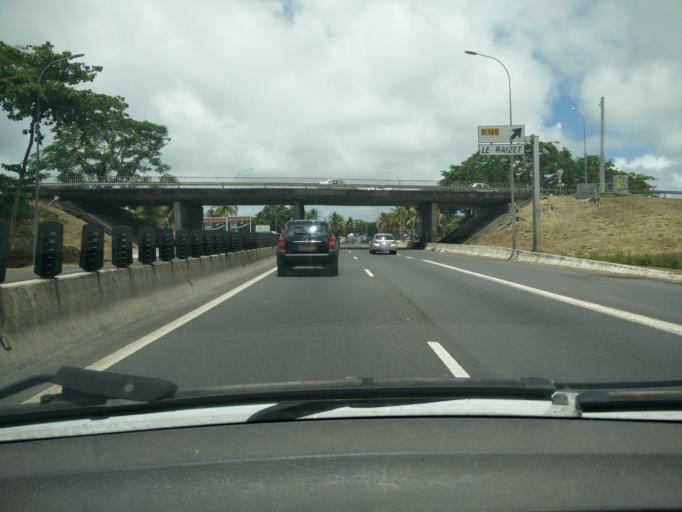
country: GP
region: Guadeloupe
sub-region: Guadeloupe
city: Pointe-a-Pitre
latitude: 16.2533
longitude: -61.5343
